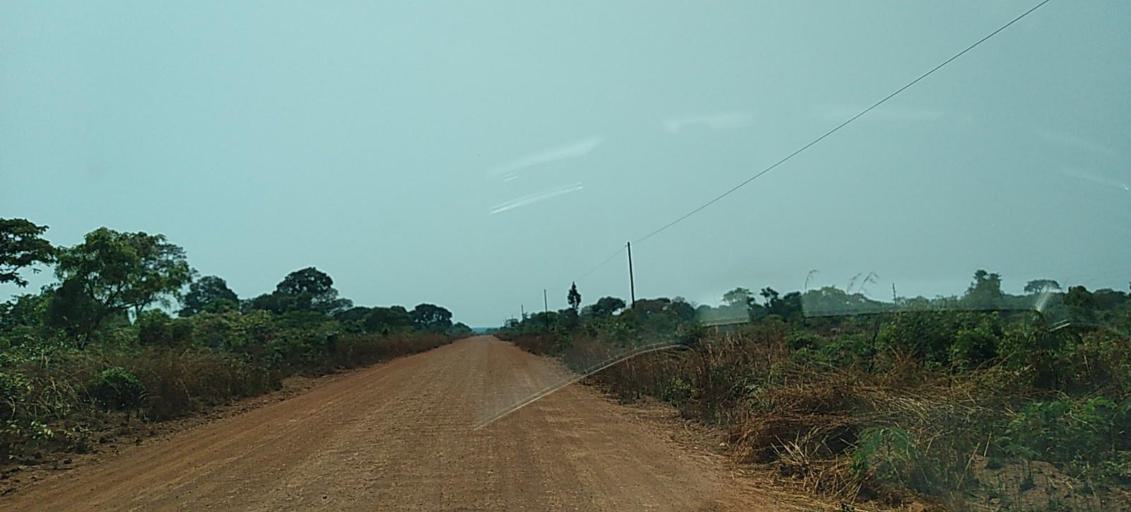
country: ZM
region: North-Western
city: Kansanshi
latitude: -11.9969
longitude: 26.6021
